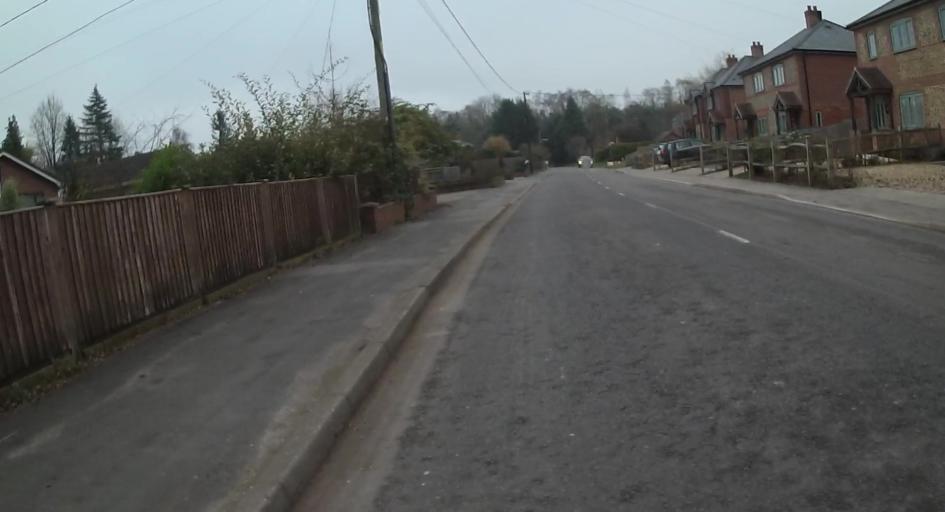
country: GB
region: England
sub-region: Hampshire
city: Kings Worthy
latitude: 51.1006
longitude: -1.3036
